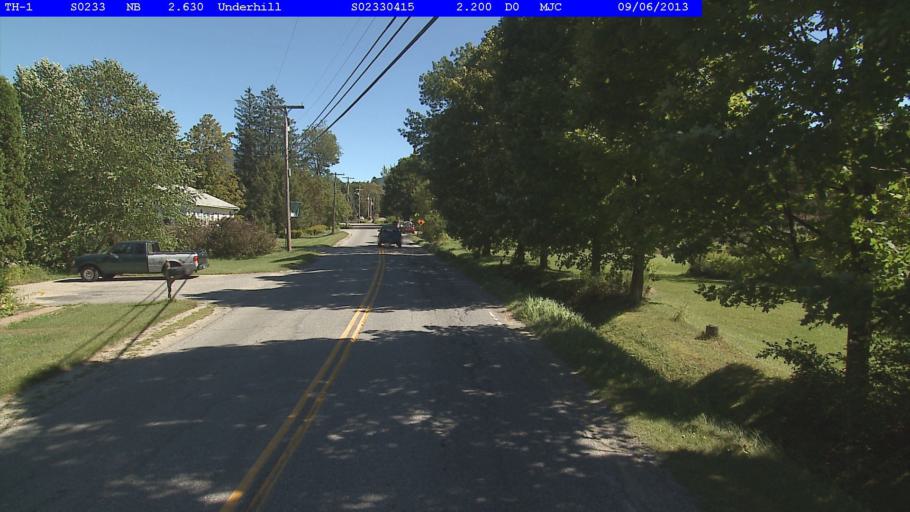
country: US
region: Vermont
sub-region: Chittenden County
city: Jericho
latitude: 44.5078
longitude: -72.9030
